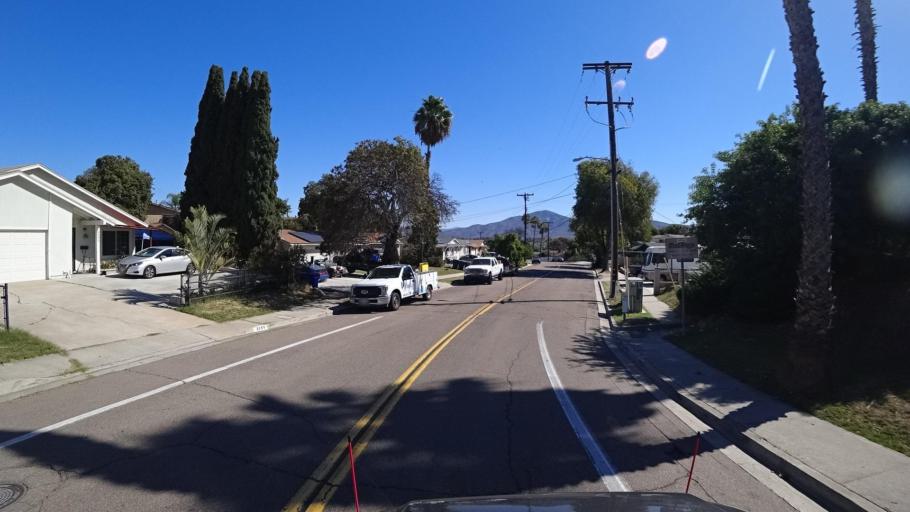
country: US
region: California
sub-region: San Diego County
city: La Presa
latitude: 32.7039
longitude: -117.0214
